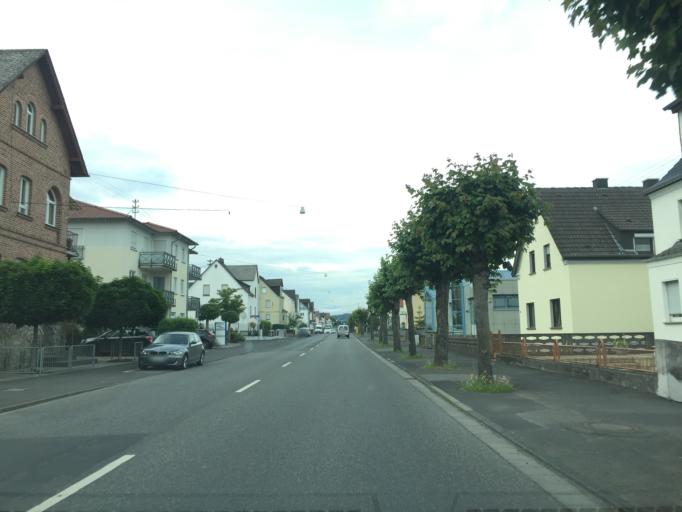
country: DE
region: Hesse
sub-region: Regierungsbezirk Giessen
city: Elz
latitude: 50.4386
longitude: 8.0378
